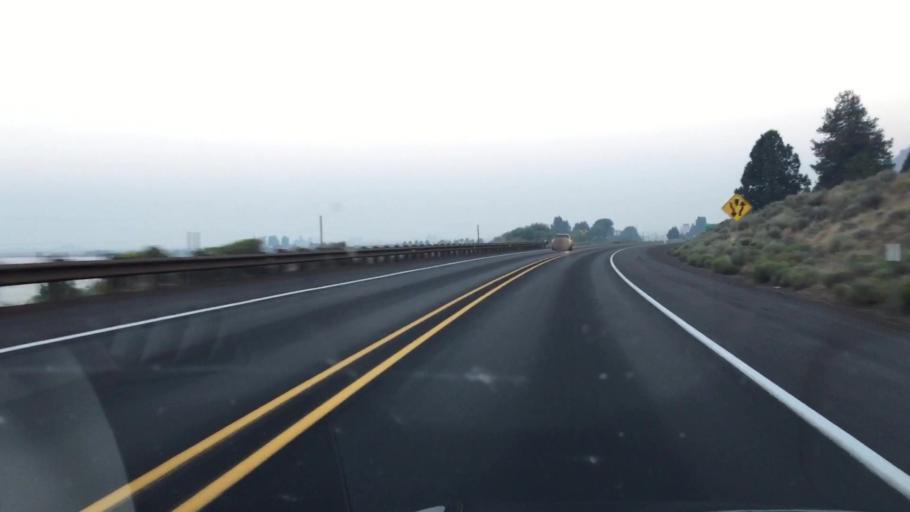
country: US
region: Oregon
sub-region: Klamath County
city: Klamath Falls
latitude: 42.4386
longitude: -121.8671
